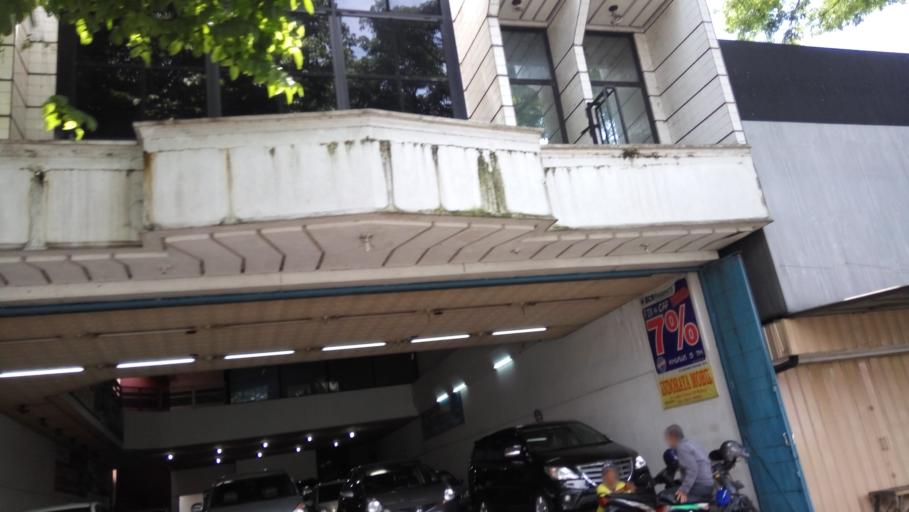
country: ID
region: East Java
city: Malang
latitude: -7.9590
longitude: 112.6375
